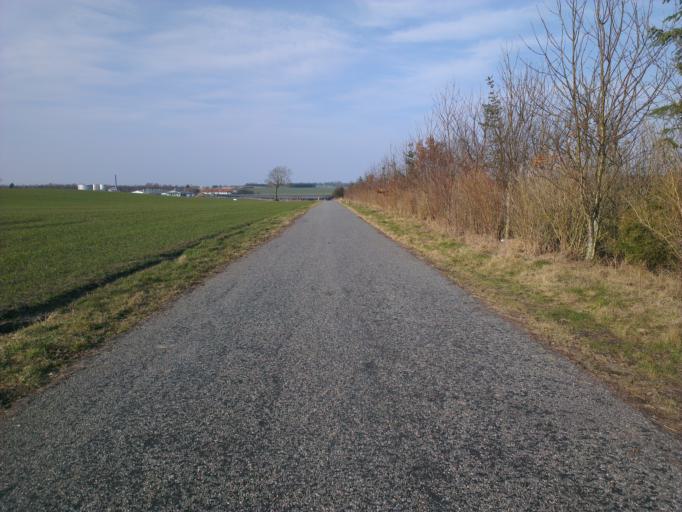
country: DK
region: Capital Region
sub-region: Frederikssund Kommune
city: Jaegerspris
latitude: 55.8242
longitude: 12.0010
